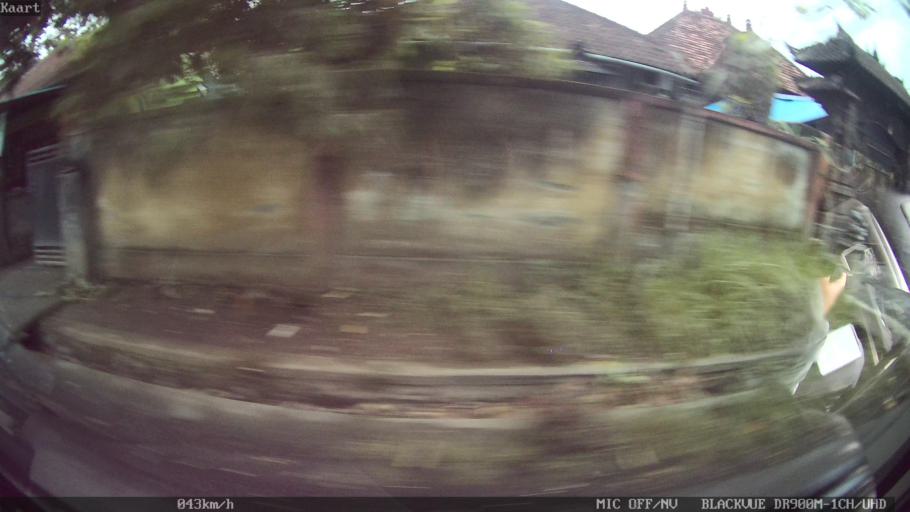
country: ID
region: Bali
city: Banjar Parekan
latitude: -8.5750
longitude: 115.2112
